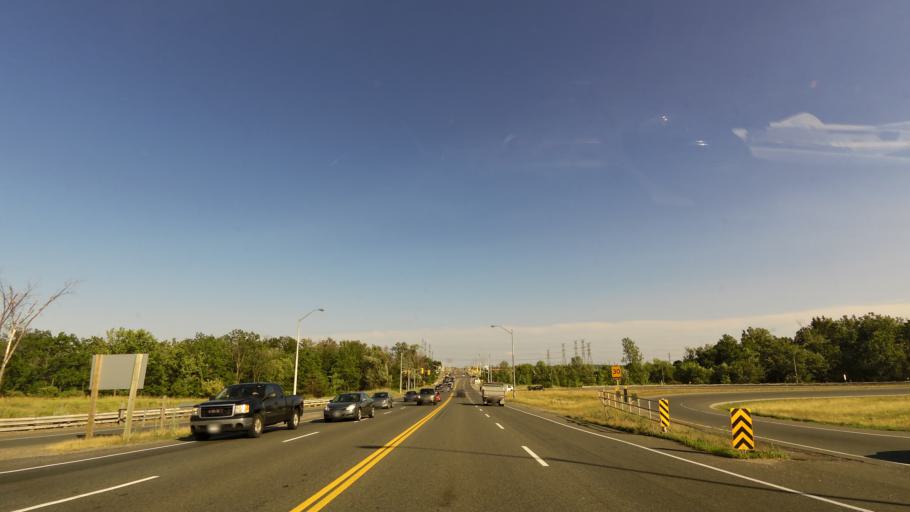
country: CA
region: Ontario
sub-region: Halton
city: Milton
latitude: 43.5703
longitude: -79.8284
